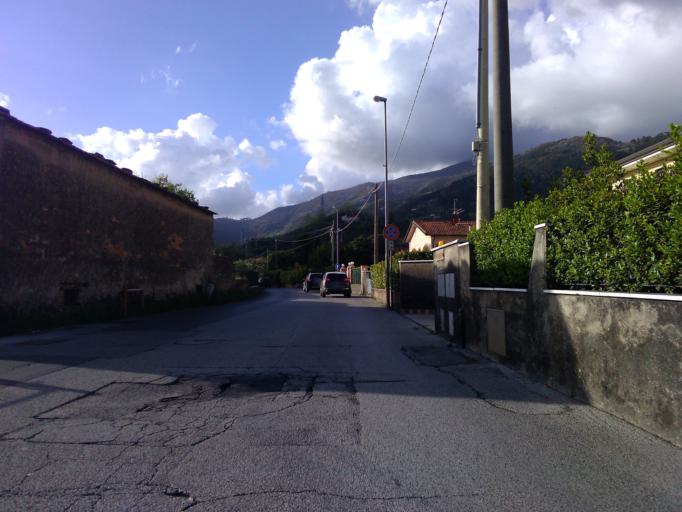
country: IT
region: Tuscany
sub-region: Provincia di Lucca
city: Ripa-Pozzi-Querceta-Ponterosso
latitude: 43.9849
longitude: 10.2091
